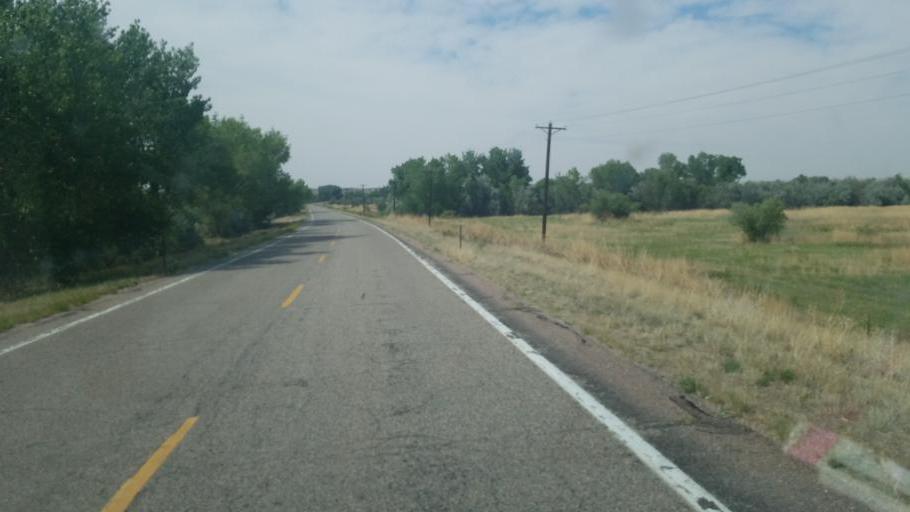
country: US
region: Colorado
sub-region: Otero County
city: Fowler
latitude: 38.2370
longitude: -104.2607
